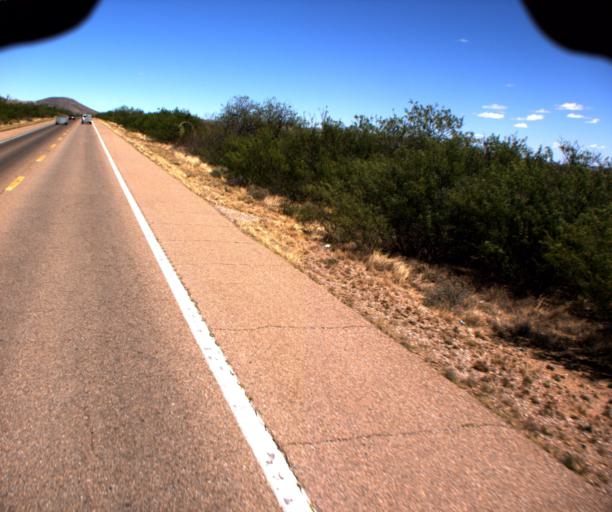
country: US
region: Arizona
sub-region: Cochise County
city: Naco
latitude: 31.3876
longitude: -109.9467
